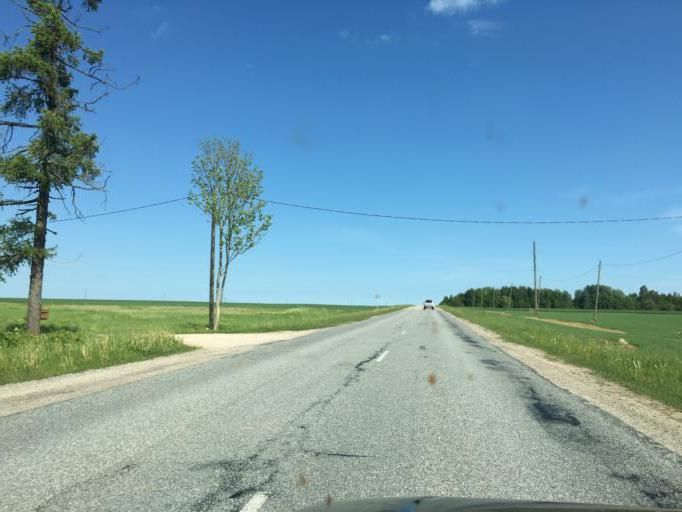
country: LV
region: Talsu Rajons
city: Valdemarpils
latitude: 57.3577
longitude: 22.4932
